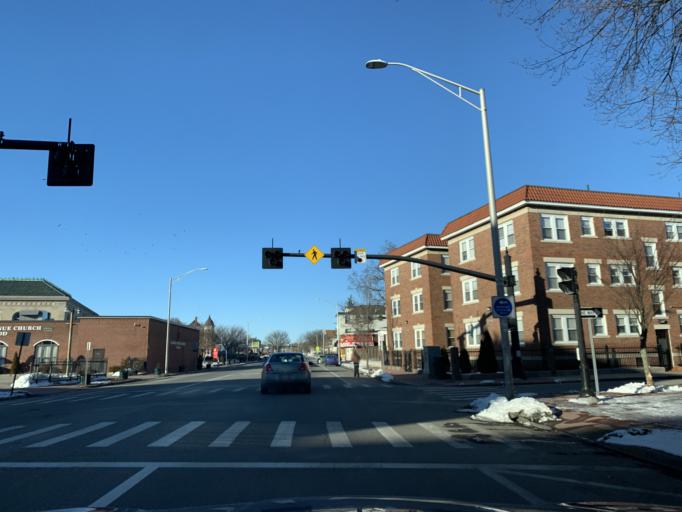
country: US
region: Rhode Island
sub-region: Providence County
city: Providence
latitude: 41.8039
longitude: -71.4256
